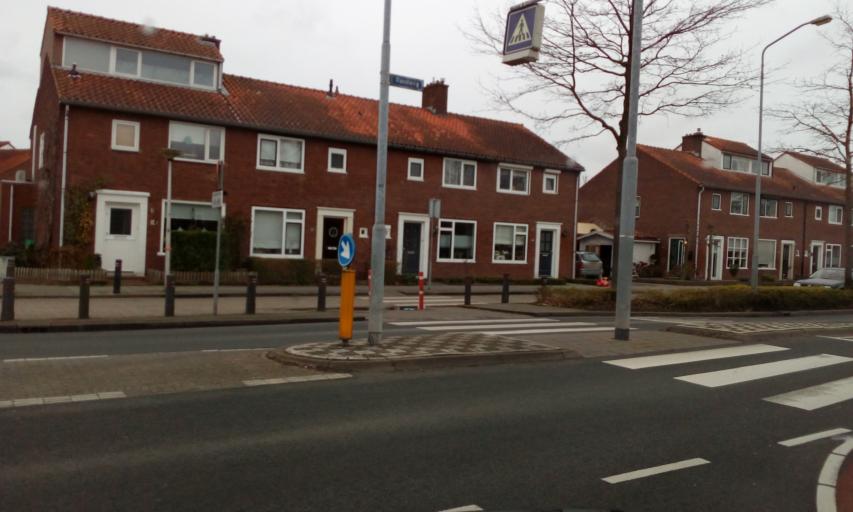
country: NL
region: South Holland
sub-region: Gemeente Alblasserdam
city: Alblasserdam
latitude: 51.8638
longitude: 4.6683
